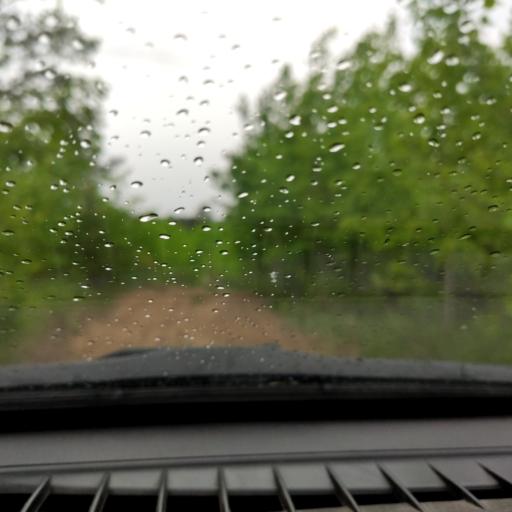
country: RU
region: Samara
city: Zhigulevsk
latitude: 53.5211
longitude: 49.5487
